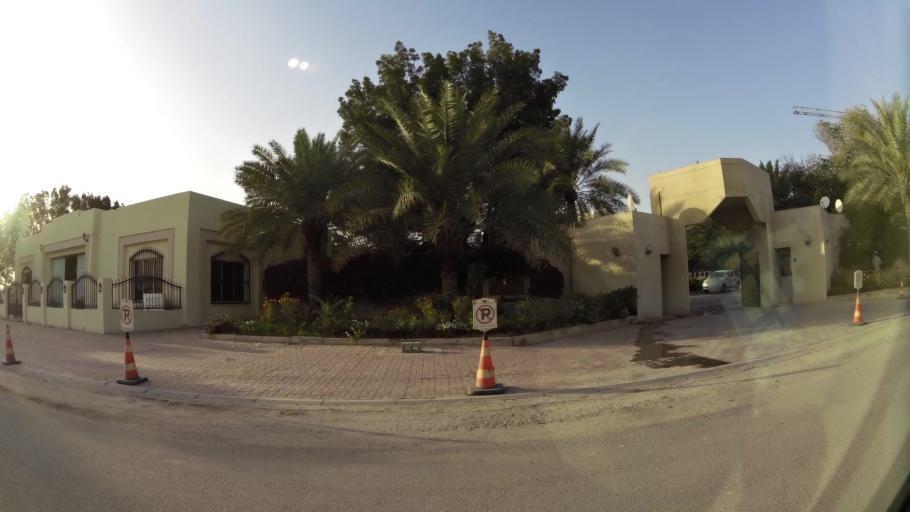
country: QA
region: Baladiyat ar Rayyan
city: Ar Rayyan
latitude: 25.3259
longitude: 51.4506
